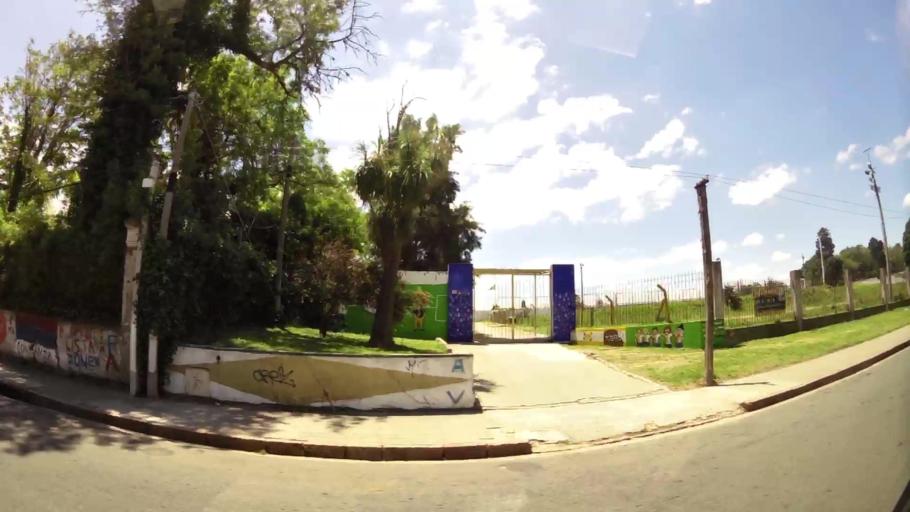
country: UY
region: Montevideo
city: Montevideo
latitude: -34.8626
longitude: -56.2097
